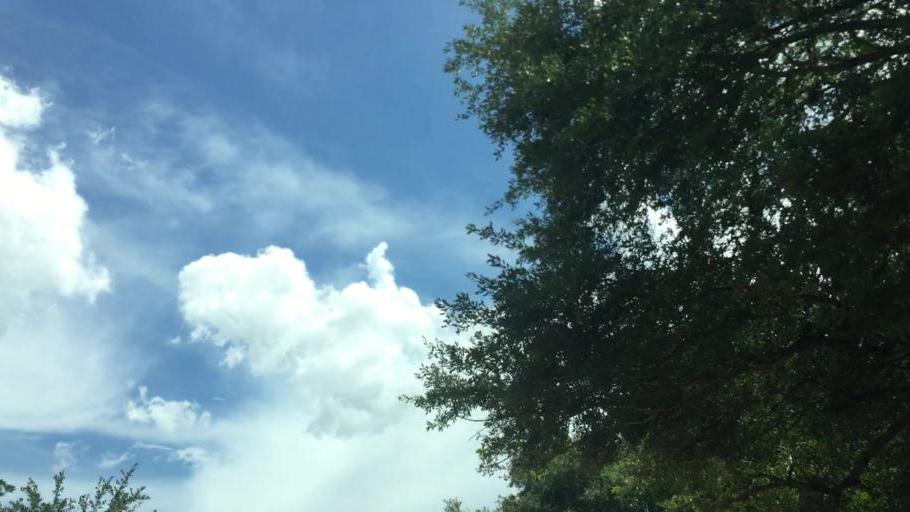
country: US
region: Texas
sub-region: Harris County
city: Bunker Hill Village
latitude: 29.7584
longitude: -95.5889
